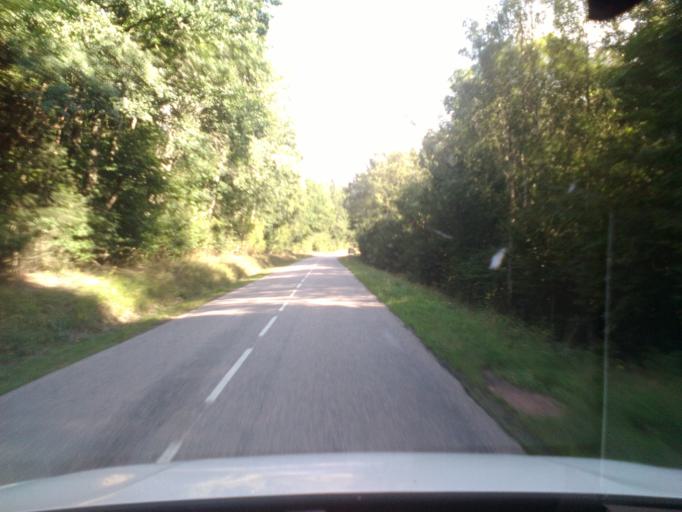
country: FR
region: Lorraine
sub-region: Departement des Vosges
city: Taintrux
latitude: 48.2351
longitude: 6.9012
